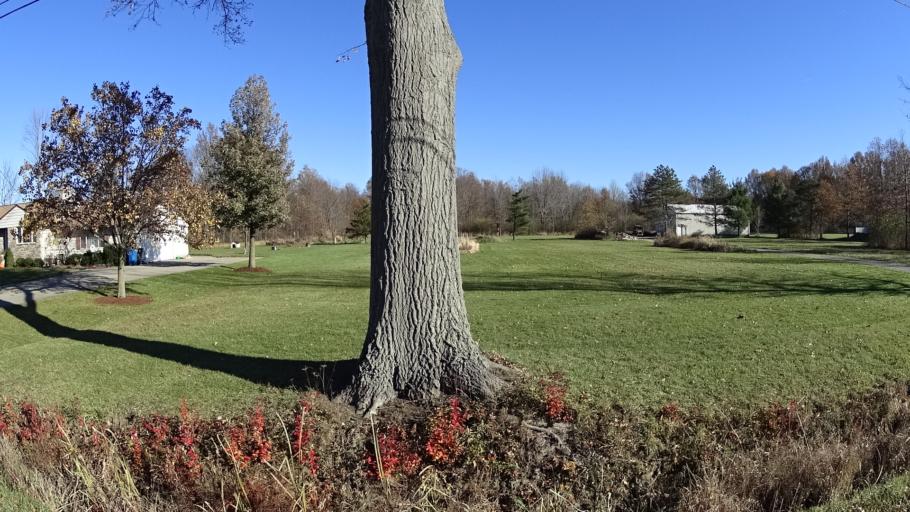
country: US
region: Ohio
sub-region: Lorain County
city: Avon Center
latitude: 41.4364
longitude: -81.9787
